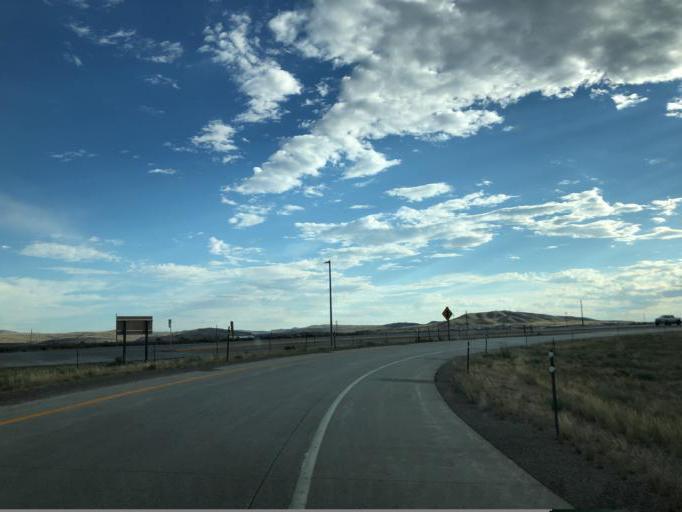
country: US
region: Wyoming
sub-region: Carbon County
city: Rawlins
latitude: 41.7880
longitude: -107.1961
